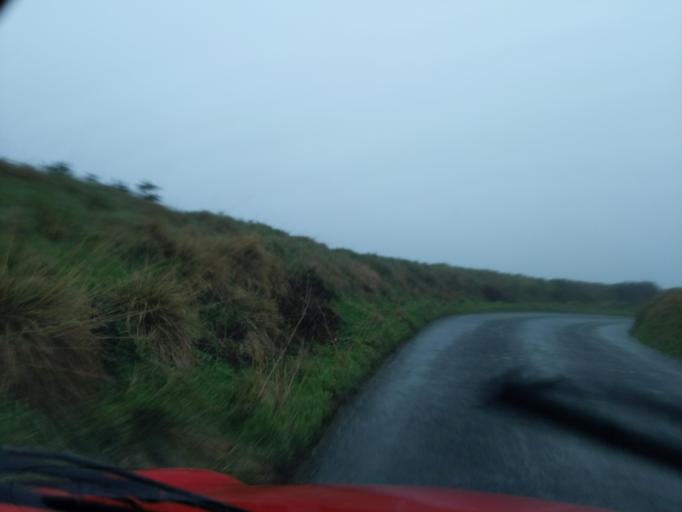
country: GB
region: England
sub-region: Cornwall
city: Camelford
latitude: 50.6529
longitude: -4.7018
